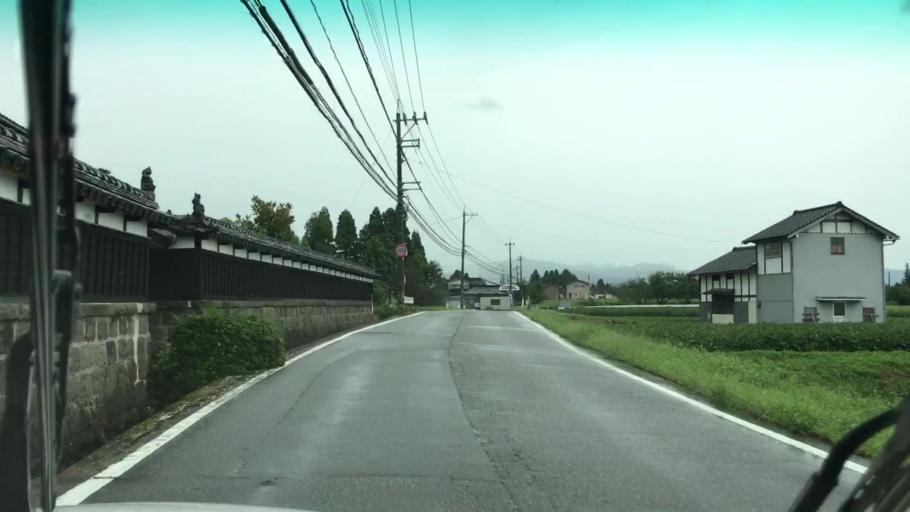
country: JP
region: Toyama
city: Kamiichi
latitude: 36.6414
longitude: 137.3205
